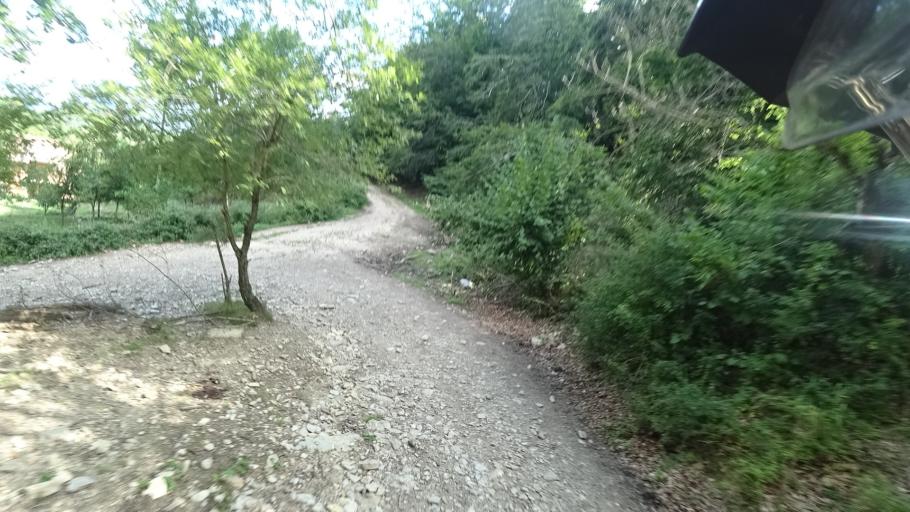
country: HR
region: Zadarska
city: Gracac
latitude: 44.3640
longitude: 16.0875
